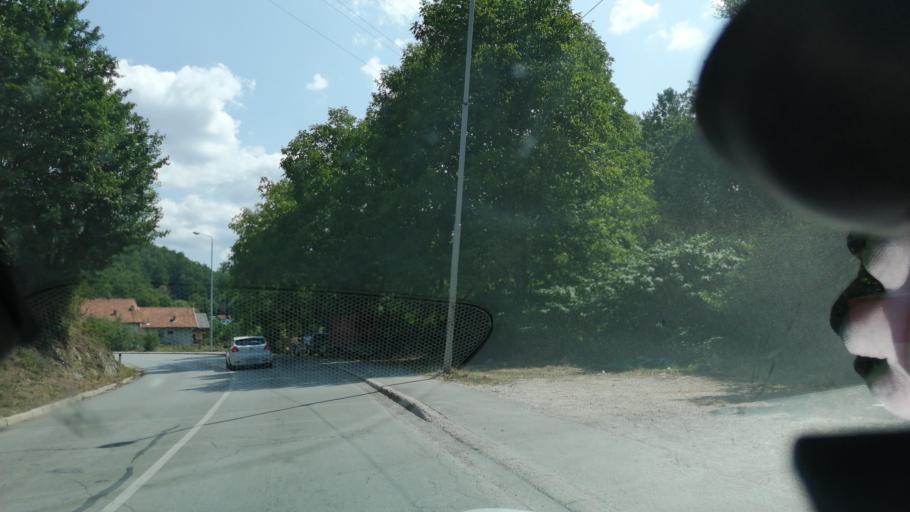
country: RS
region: Central Serbia
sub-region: Moravicki Okrug
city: Ivanjica
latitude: 43.5996
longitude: 20.2256
